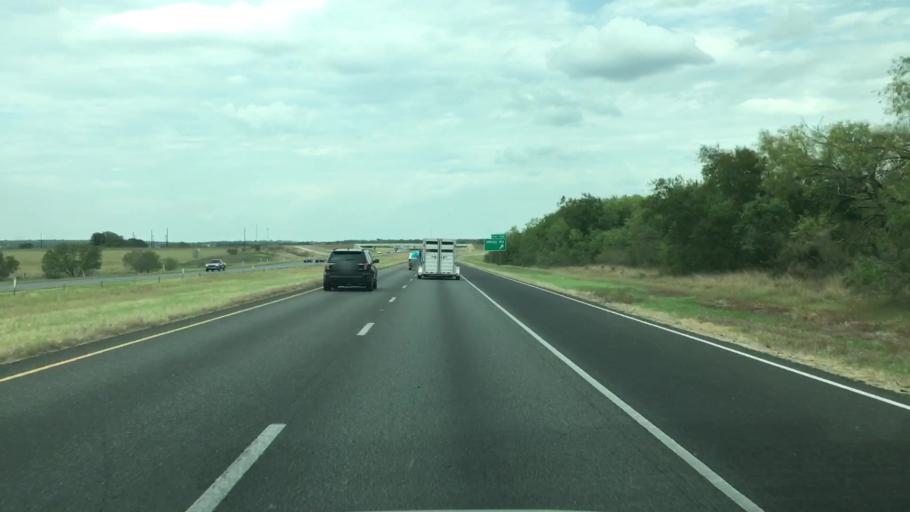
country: US
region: Texas
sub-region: Bexar County
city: Elmendorf
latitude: 29.1358
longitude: -98.4294
